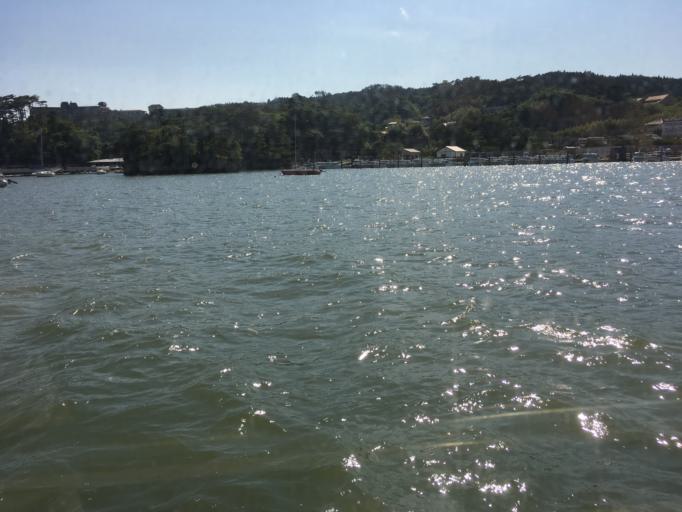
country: JP
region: Miyagi
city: Matsushima
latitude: 38.3682
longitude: 141.0634
